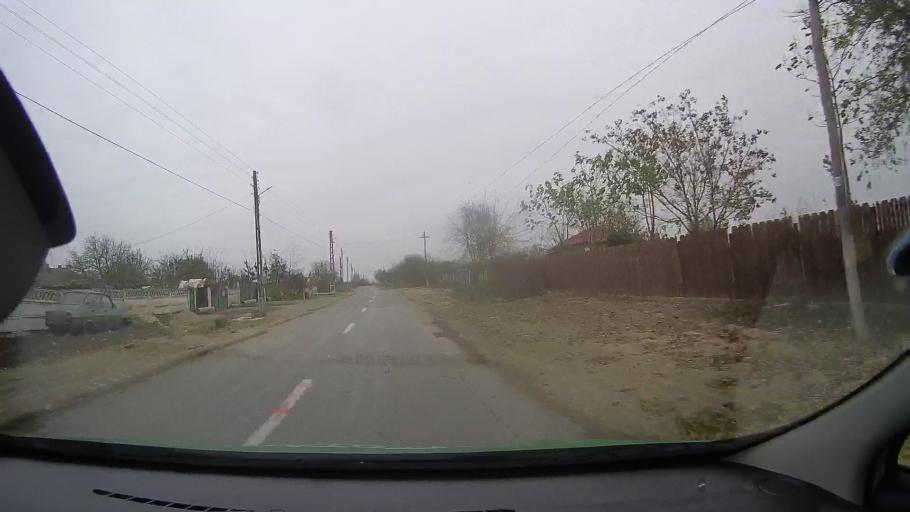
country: RO
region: Constanta
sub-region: Comuna Vulturu
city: Vulturu
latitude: 44.6528
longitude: 28.2678
